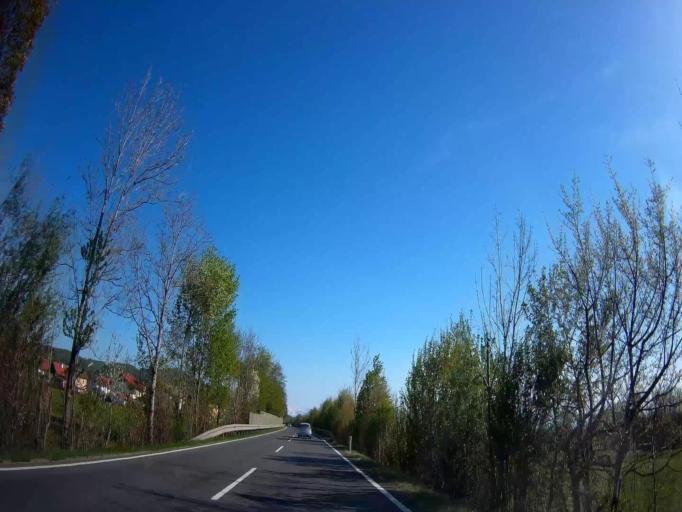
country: AT
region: Salzburg
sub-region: Politischer Bezirk Salzburg-Umgebung
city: Anthering
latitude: 47.8818
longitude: 13.0028
